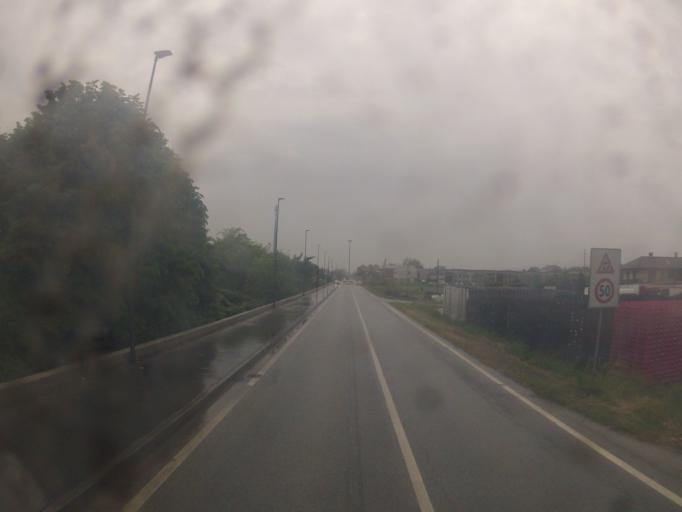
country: IT
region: Piedmont
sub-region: Provincia di Torino
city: La Loggia
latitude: 44.9446
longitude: 7.6699
